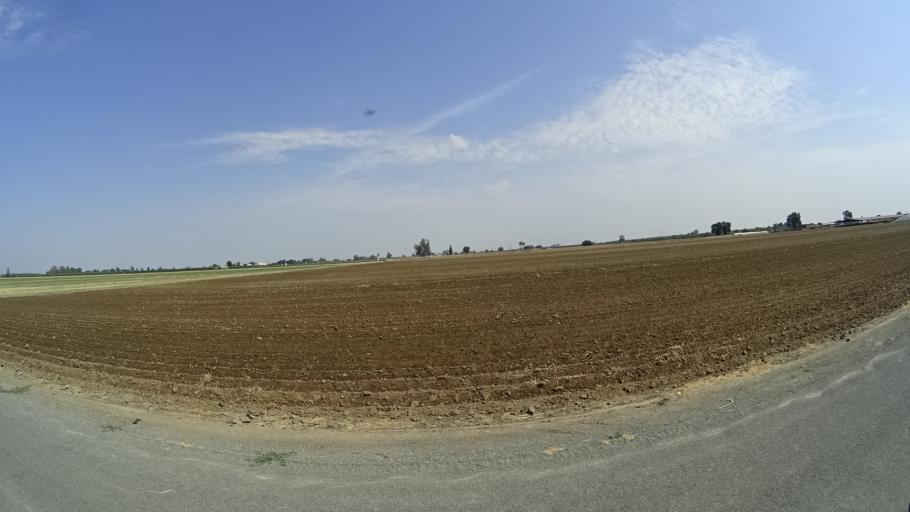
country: US
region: California
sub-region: Fresno County
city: Riverdale
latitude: 36.3947
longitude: -119.7865
